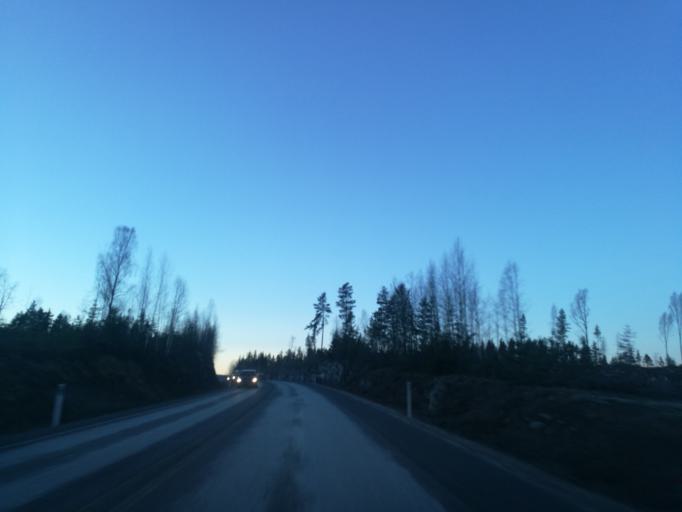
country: NO
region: Hedmark
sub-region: Eidskog
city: Skotterud
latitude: 59.9763
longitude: 12.1265
